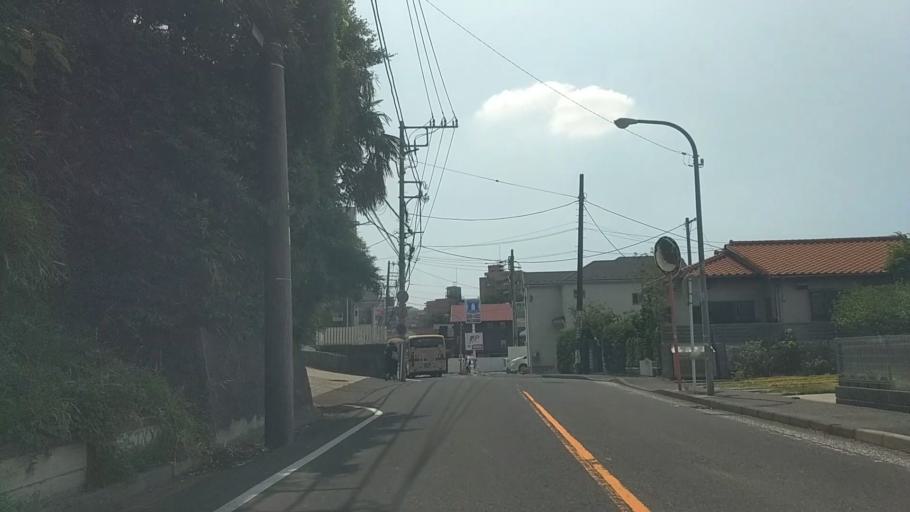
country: JP
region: Kanagawa
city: Yokohama
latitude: 35.5022
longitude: 139.6542
